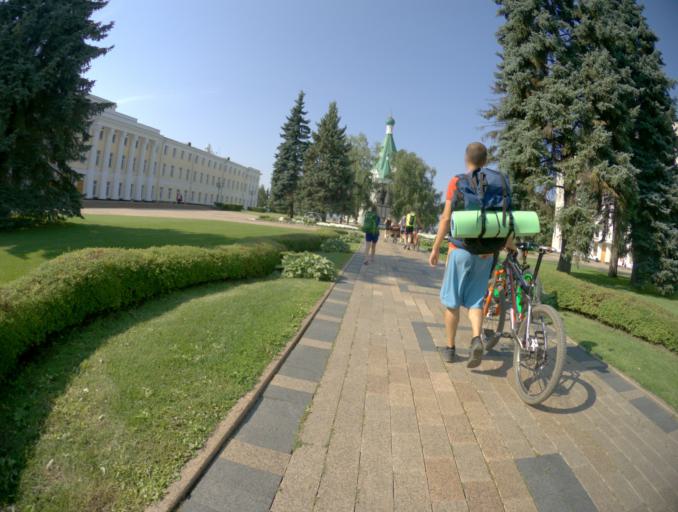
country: RU
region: Nizjnij Novgorod
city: Nizhniy Novgorod
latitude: 56.3274
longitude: 44.0023
